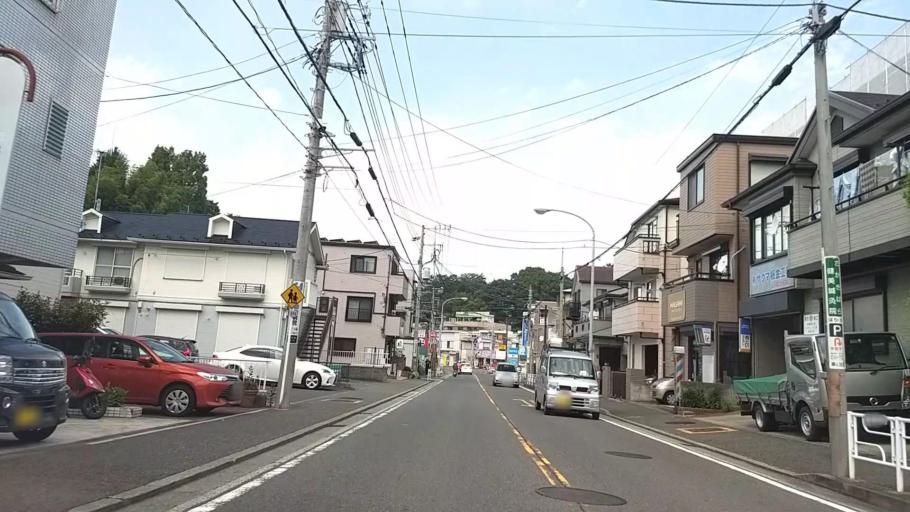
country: JP
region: Kanagawa
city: Yokohama
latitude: 35.4155
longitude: 139.5754
